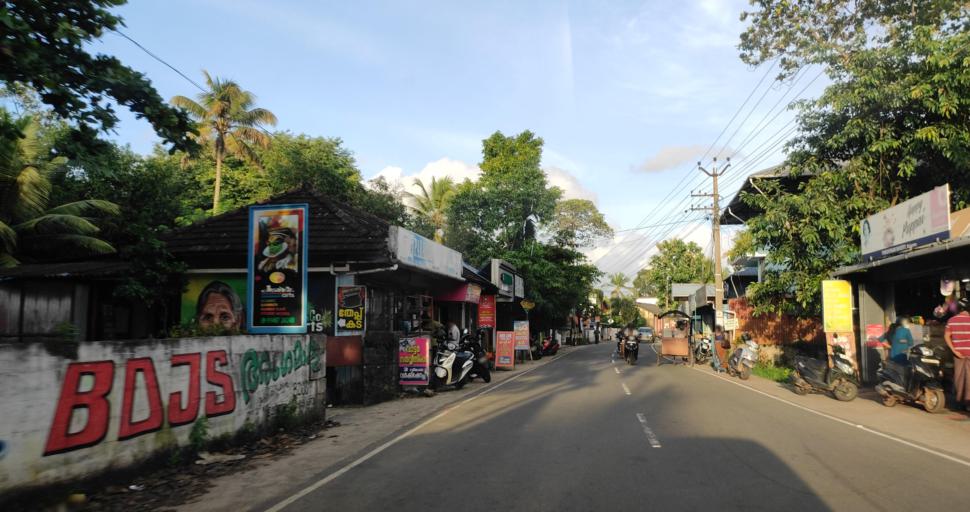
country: IN
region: Kerala
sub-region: Alappuzha
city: Shertallai
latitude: 9.6070
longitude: 76.3554
